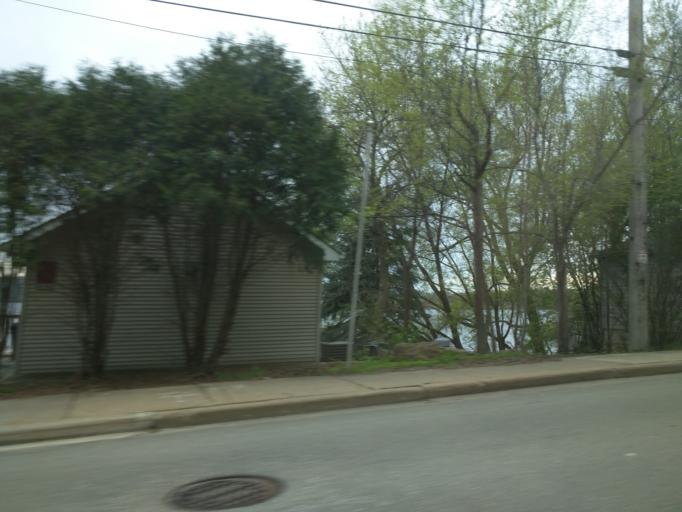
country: US
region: Minnesota
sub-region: Wabasha County
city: Lake City
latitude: 44.5620
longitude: -92.3116
